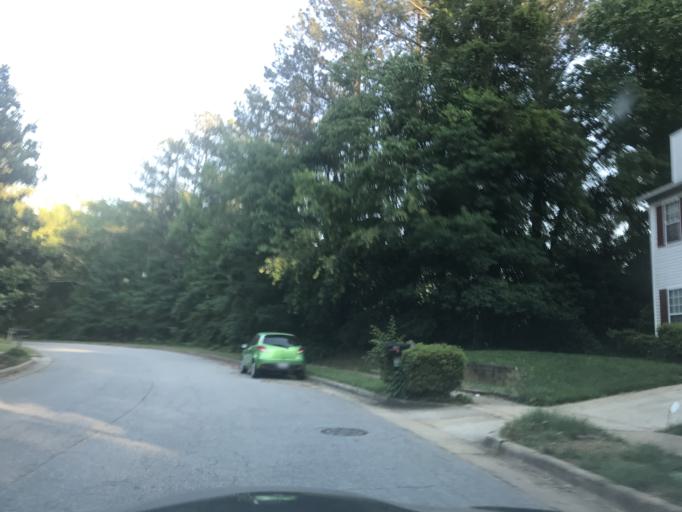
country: US
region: North Carolina
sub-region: Wake County
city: West Raleigh
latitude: 35.7503
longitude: -78.6688
